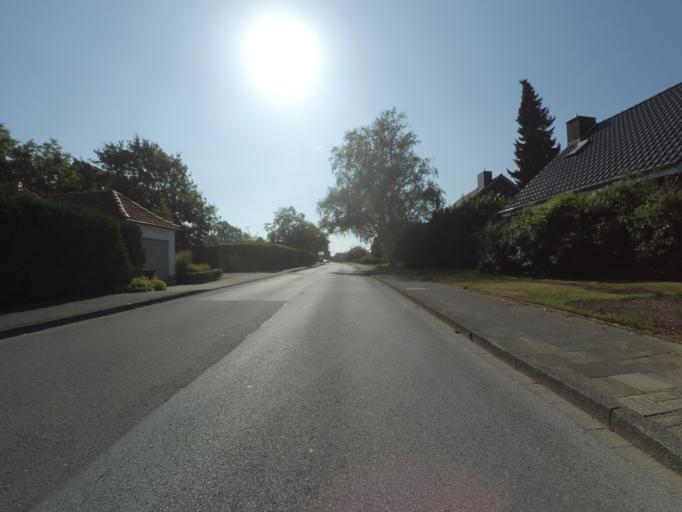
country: DE
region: North Rhine-Westphalia
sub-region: Regierungsbezirk Munster
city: Steinfurt
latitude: 52.1404
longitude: 7.3328
